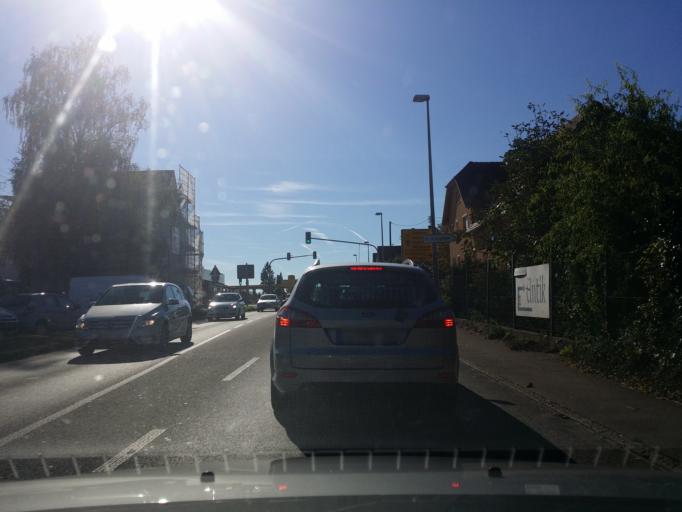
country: DE
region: Baden-Wuerttemberg
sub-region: Tuebingen Region
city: Ofterdingen
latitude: 48.4179
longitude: 9.0372
